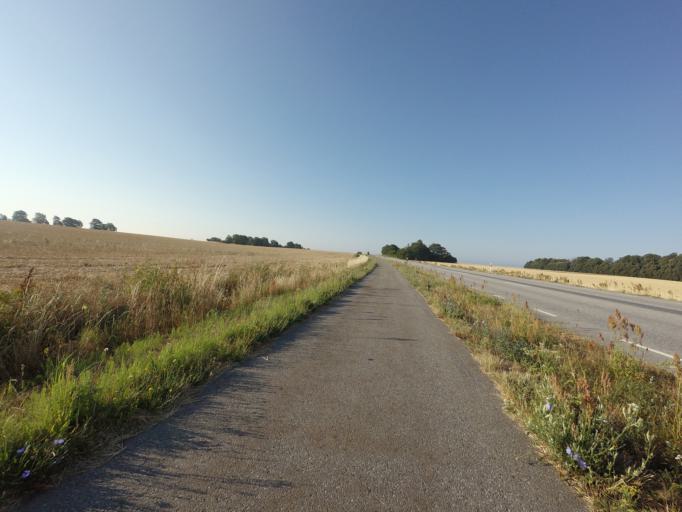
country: SE
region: Skane
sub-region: Helsingborg
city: Glumslov
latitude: 55.9209
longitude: 12.8159
